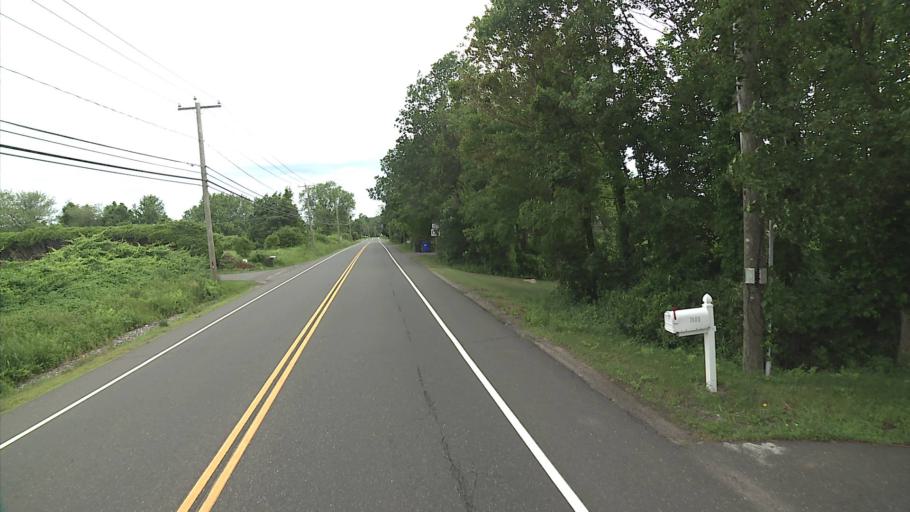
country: US
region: Connecticut
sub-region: Litchfield County
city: Watertown
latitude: 41.6438
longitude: -73.1473
